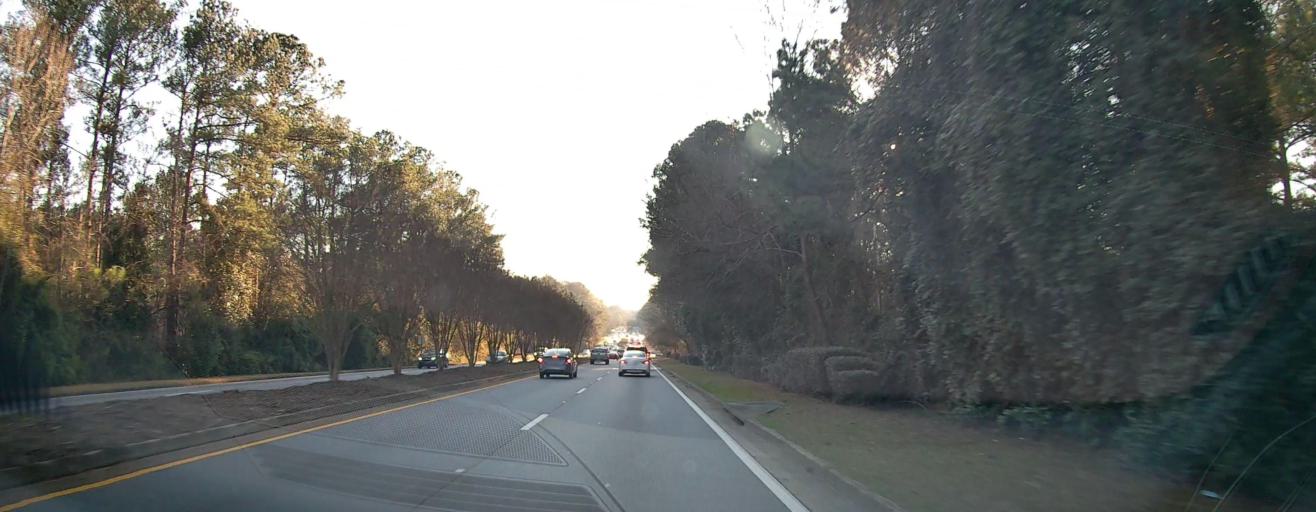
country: US
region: Georgia
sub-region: Fayette County
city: Peachtree City
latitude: 33.4115
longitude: -84.5647
